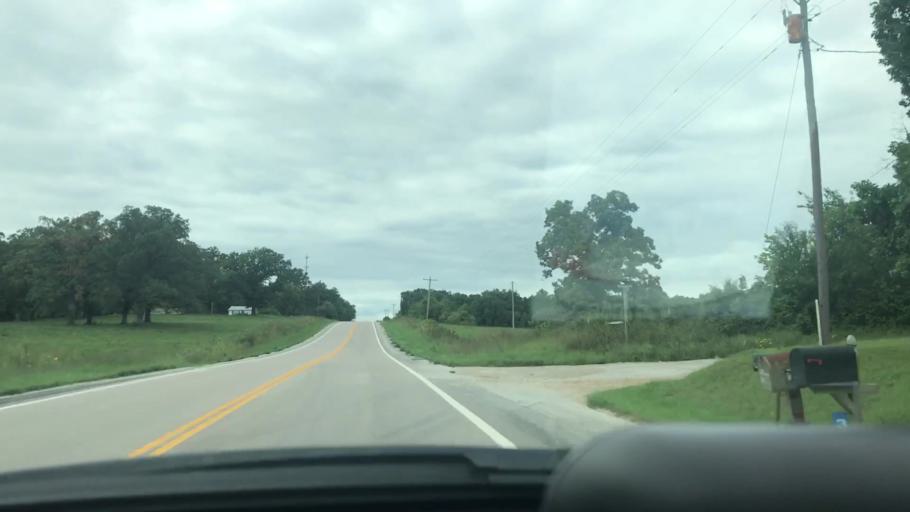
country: US
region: Missouri
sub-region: Benton County
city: Warsaw
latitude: 38.1391
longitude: -93.2855
